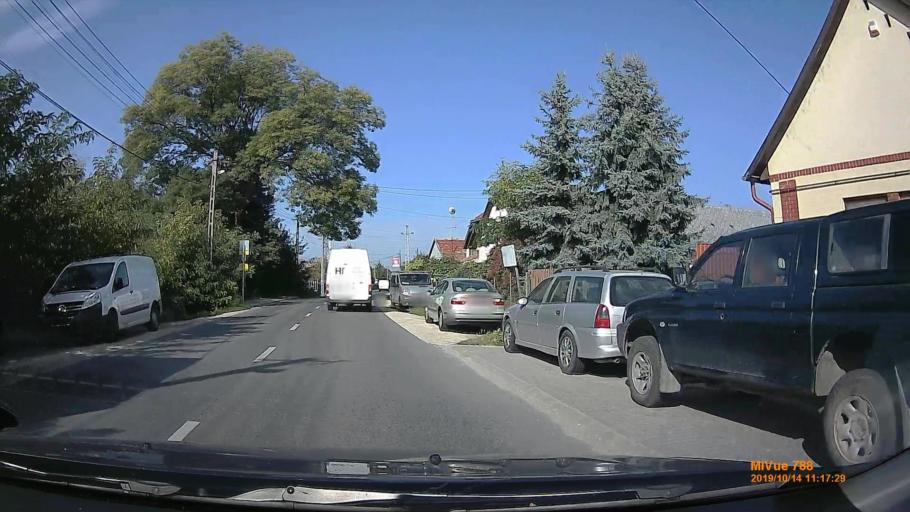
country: HU
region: Pest
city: Gyomro
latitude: 47.4166
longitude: 19.3930
